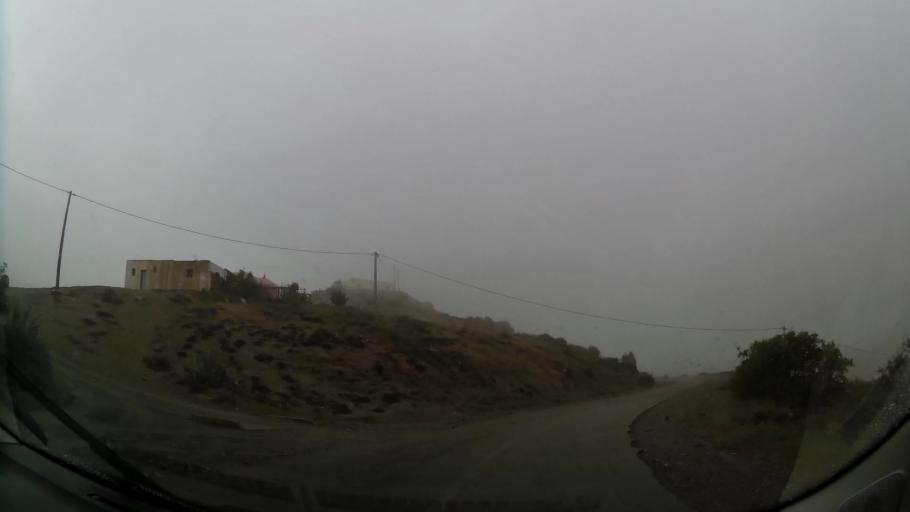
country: MA
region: Taza-Al Hoceima-Taounate
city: Imzourene
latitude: 35.1213
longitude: -3.7730
